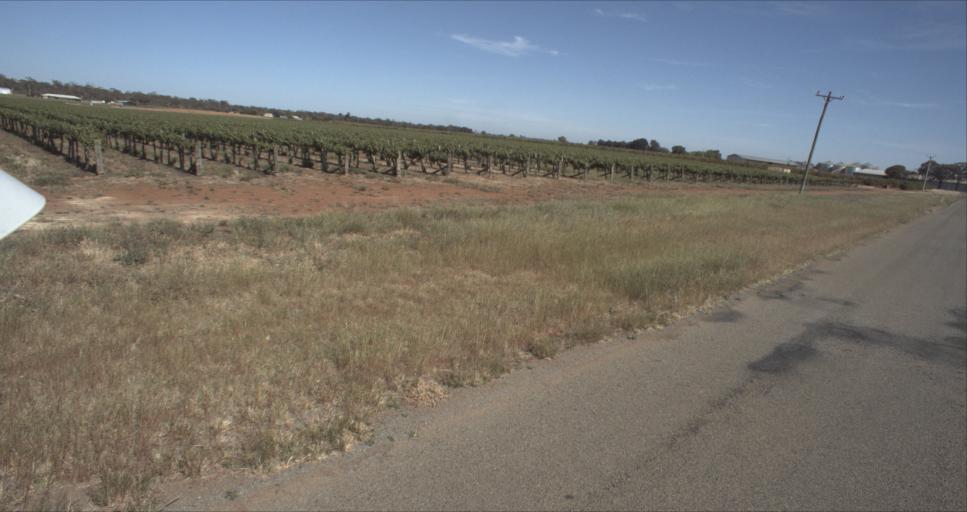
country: AU
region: New South Wales
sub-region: Leeton
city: Leeton
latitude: -34.5615
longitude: 146.4691
